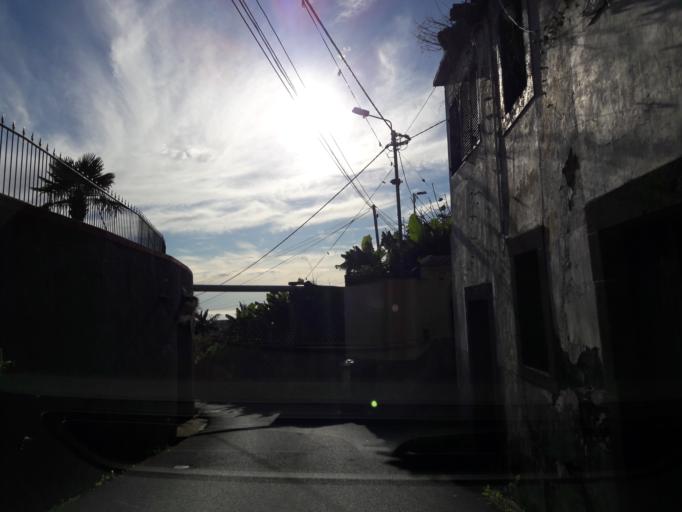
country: PT
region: Madeira
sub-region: Funchal
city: Nossa Senhora do Monte
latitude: 32.6673
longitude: -16.9222
